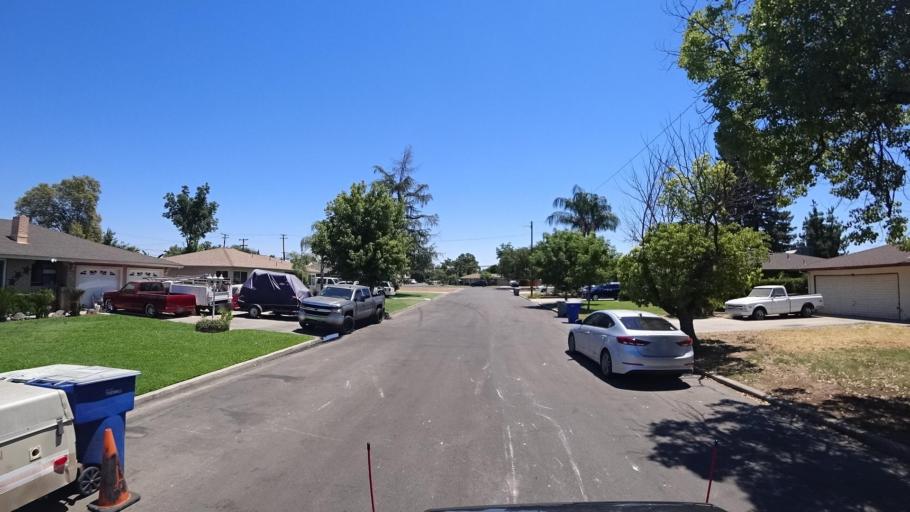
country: US
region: California
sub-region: Fresno County
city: Fresno
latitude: 36.7768
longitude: -119.7419
